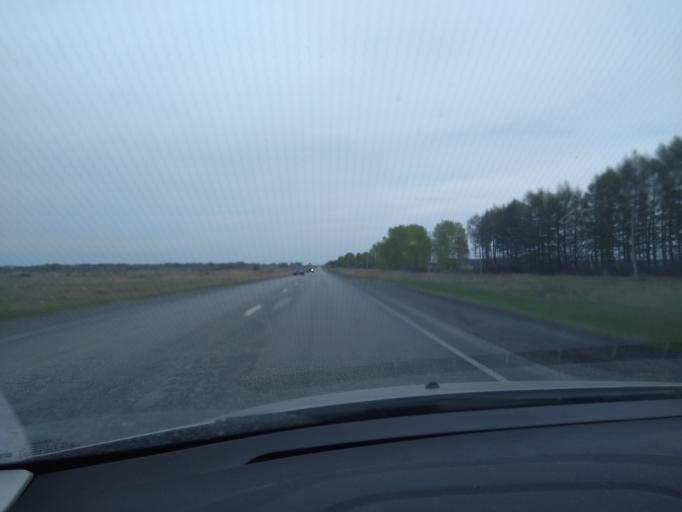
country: RU
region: Sverdlovsk
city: Talitsa
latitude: 57.0600
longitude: 63.5399
